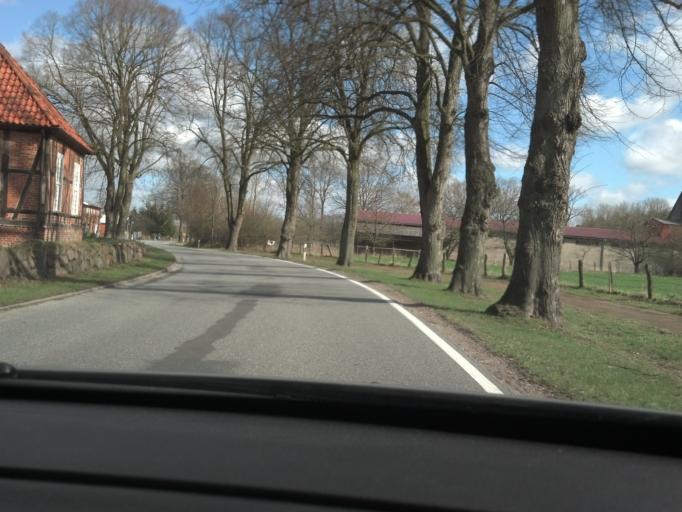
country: DE
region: Schleswig-Holstein
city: Langenlehsten
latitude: 53.4516
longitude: 10.7709
